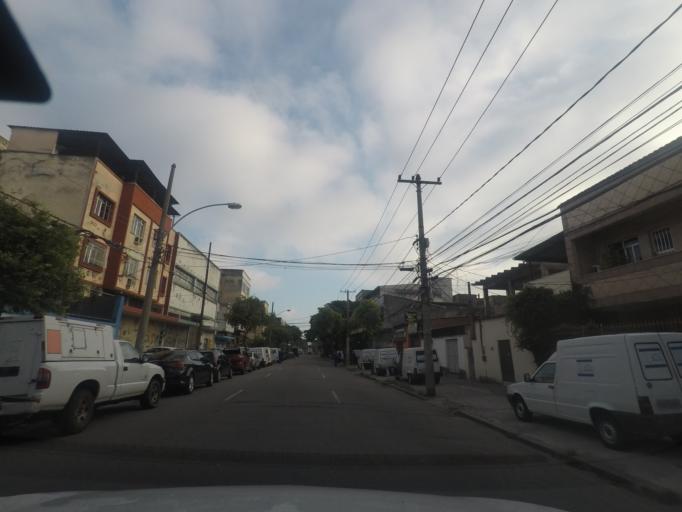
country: BR
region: Rio de Janeiro
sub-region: Duque De Caxias
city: Duque de Caxias
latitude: -22.8376
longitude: -43.2796
